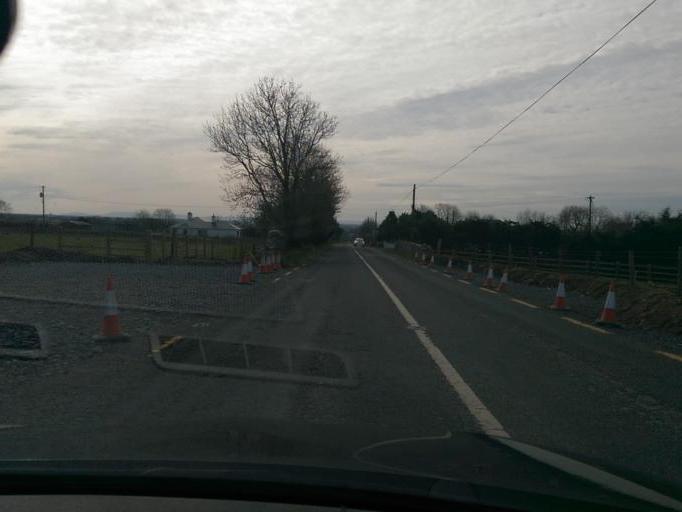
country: IE
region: Connaught
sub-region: County Galway
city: Tuam
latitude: 53.4063
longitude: -8.8235
